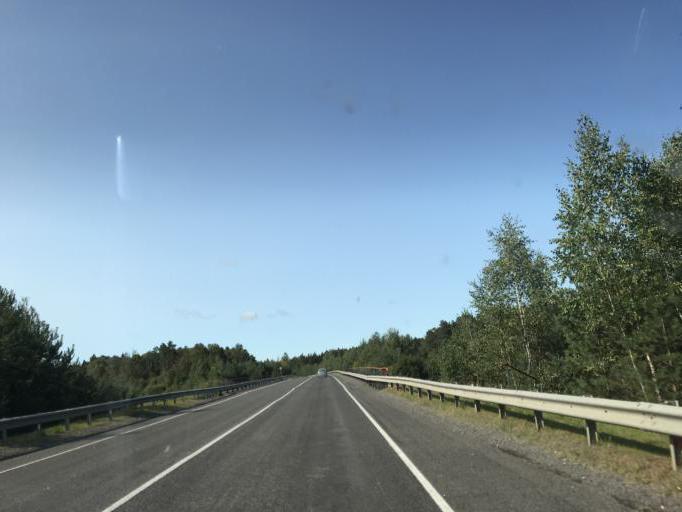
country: BY
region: Mogilev
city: Myazhysyatki
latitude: 53.8084
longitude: 30.2161
